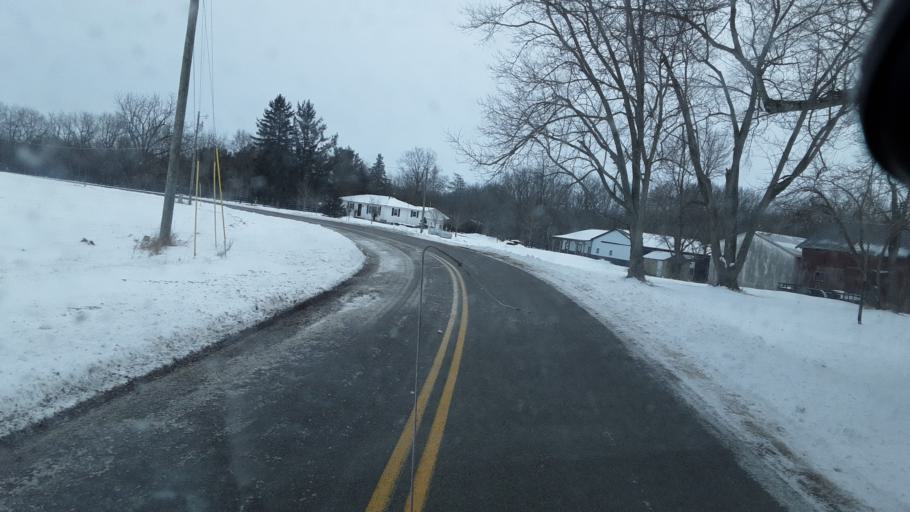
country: US
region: Ohio
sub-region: Madison County
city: Plain City
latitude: 40.1336
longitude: -83.3165
